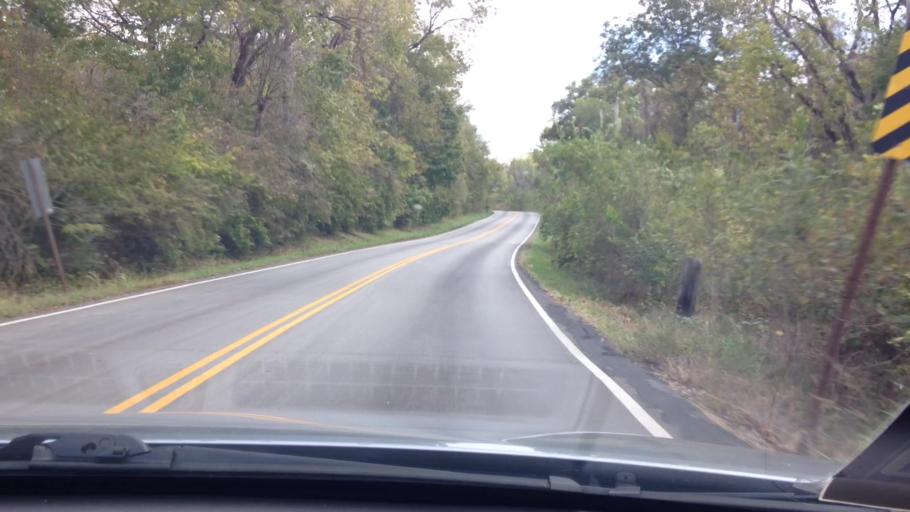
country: US
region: Missouri
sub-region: Platte County
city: Weatherby Lake
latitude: 39.2483
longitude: -94.7927
